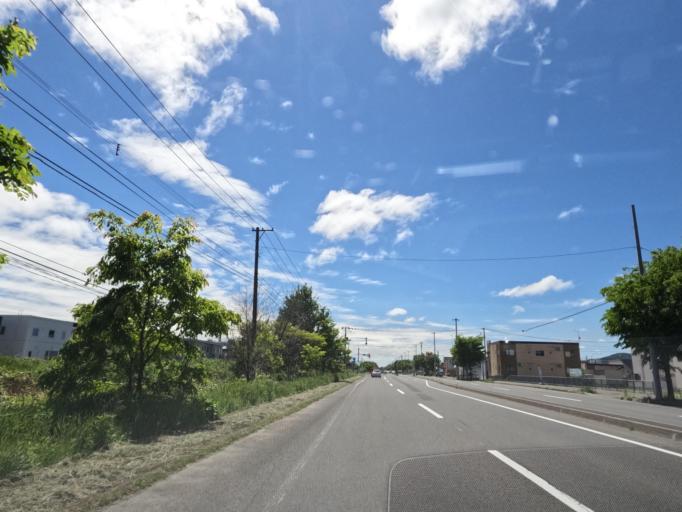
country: JP
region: Hokkaido
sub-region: Asahikawa-shi
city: Asahikawa
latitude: 43.7408
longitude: 142.3599
